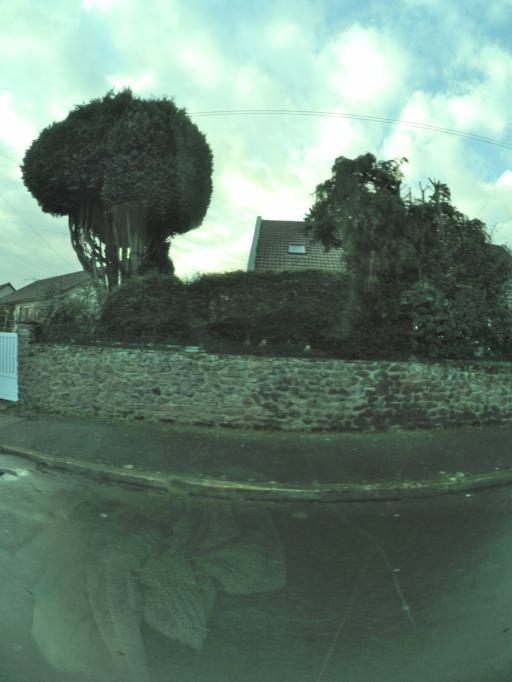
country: FR
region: Pays de la Loire
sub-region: Departement de la Sarthe
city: La Milesse
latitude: 48.0656
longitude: 0.1359
